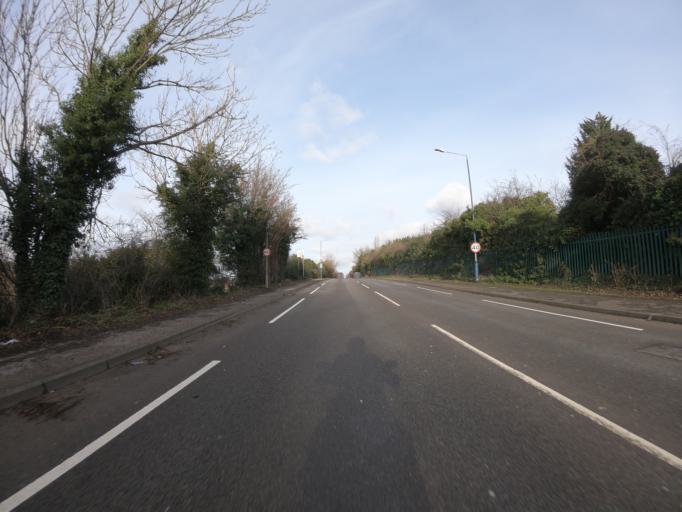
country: GB
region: England
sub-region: Kent
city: Gravesend
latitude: 51.4211
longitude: 0.3611
